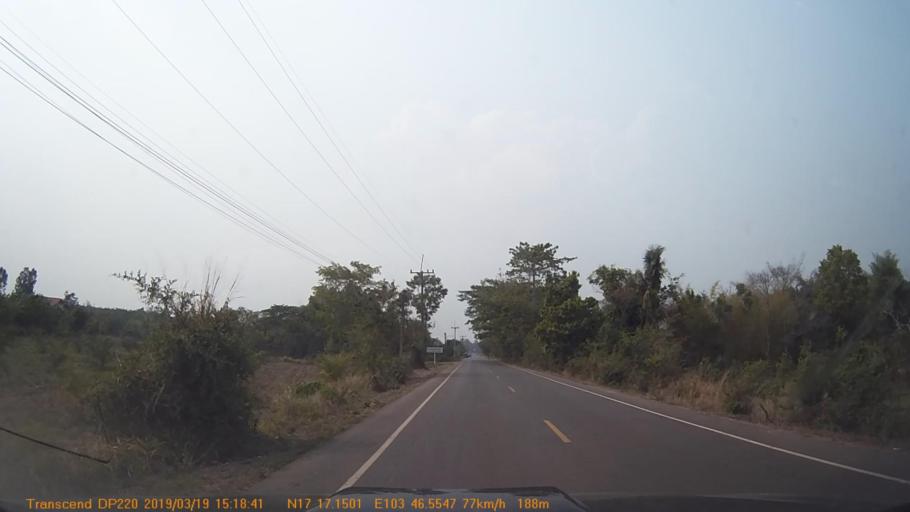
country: TH
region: Sakon Nakhon
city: Phanna Nikhom
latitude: 17.2861
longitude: 103.7758
